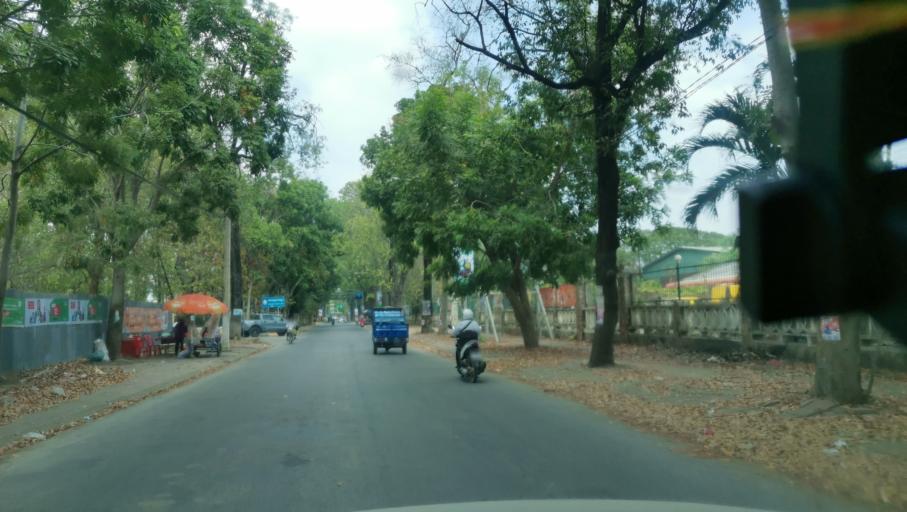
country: KH
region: Battambang
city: Battambang
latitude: 13.0889
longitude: 103.2000
